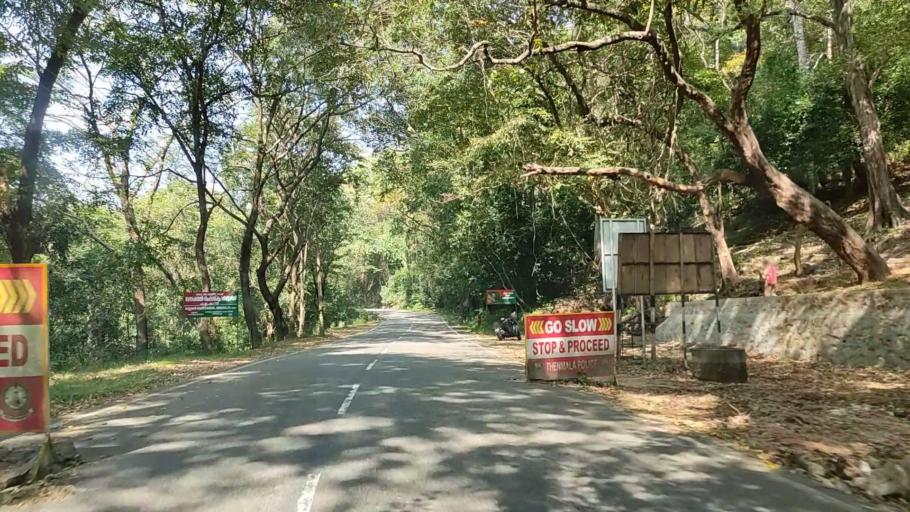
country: IN
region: Kerala
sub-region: Kollam
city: Punalur
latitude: 8.9620
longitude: 77.0679
